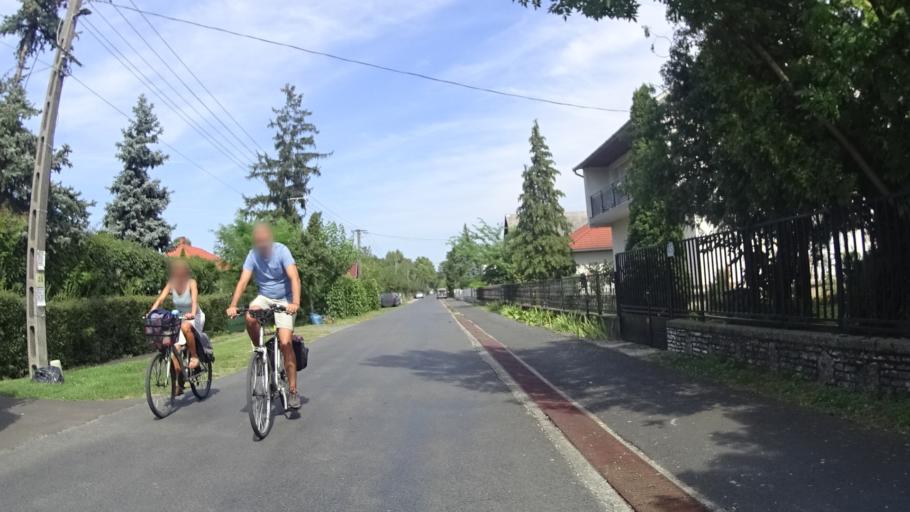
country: HU
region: Somogy
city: Balatonboglar
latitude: 46.7738
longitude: 17.6385
